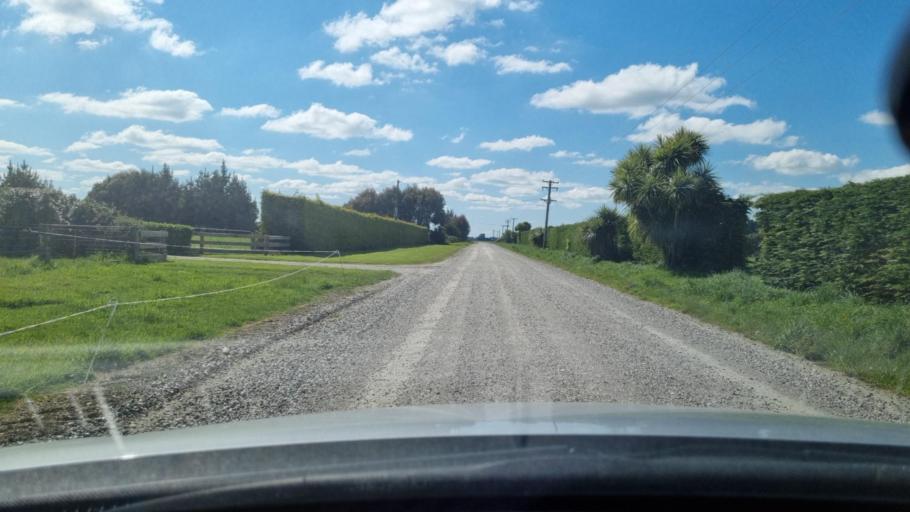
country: NZ
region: Southland
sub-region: Invercargill City
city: Invercargill
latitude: -46.3742
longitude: 168.2985
